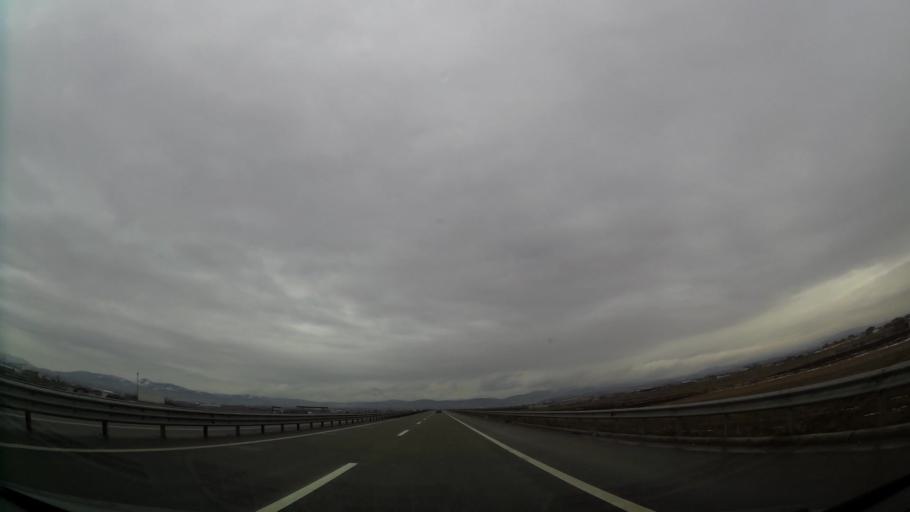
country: XK
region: Pristina
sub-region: Lipjan
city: Lipljan
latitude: 42.5307
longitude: 21.1523
